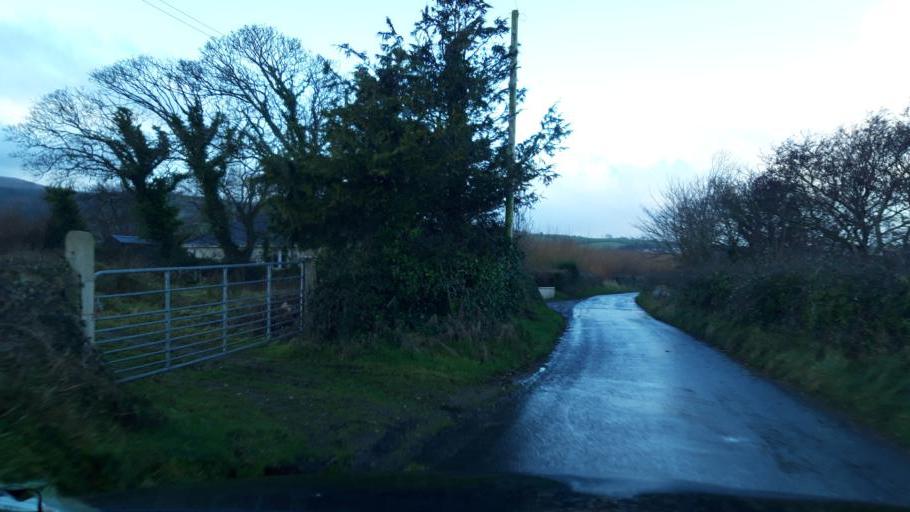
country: GB
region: Northern Ireland
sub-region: Moyle District
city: Ballycastle
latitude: 55.1975
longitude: -6.2149
